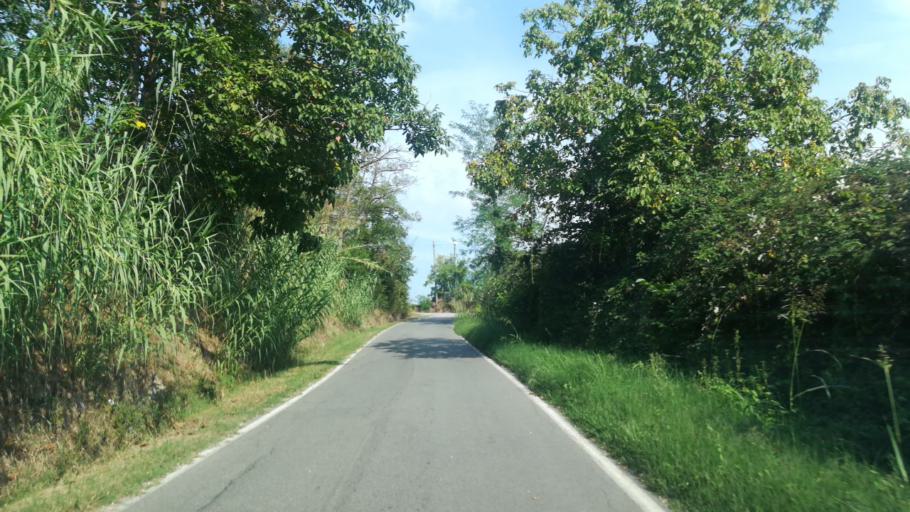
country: IT
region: Piedmont
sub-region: Provincia di Alessandria
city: San Salvatore Monferrato
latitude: 44.9999
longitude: 8.5480
